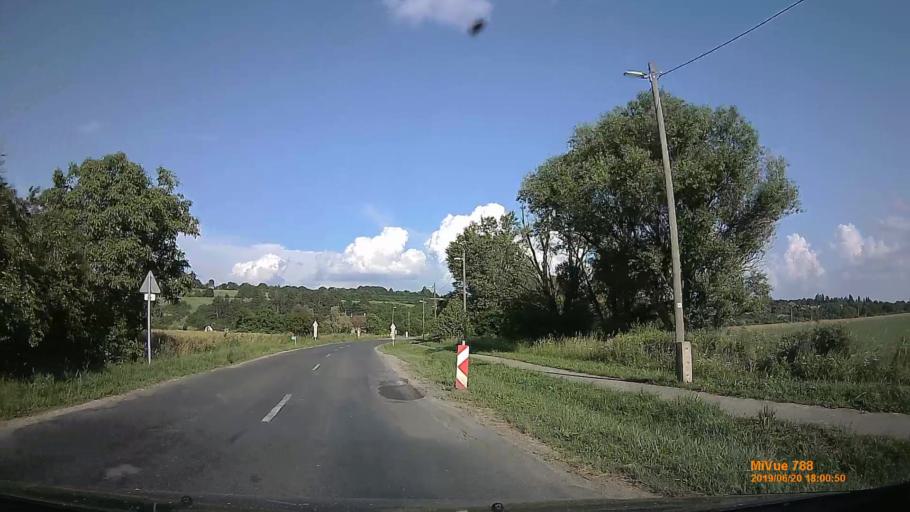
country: HU
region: Baranya
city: Buekkoesd
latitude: 46.0861
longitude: 17.9850
